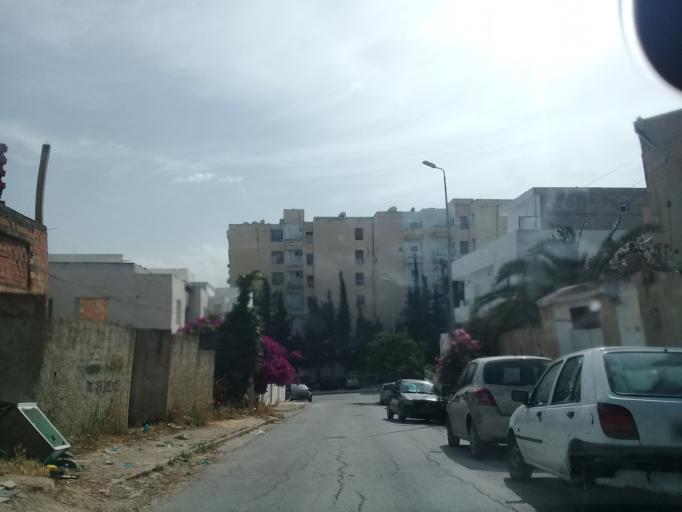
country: TN
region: Tunis
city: Tunis
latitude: 36.8512
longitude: 10.1582
